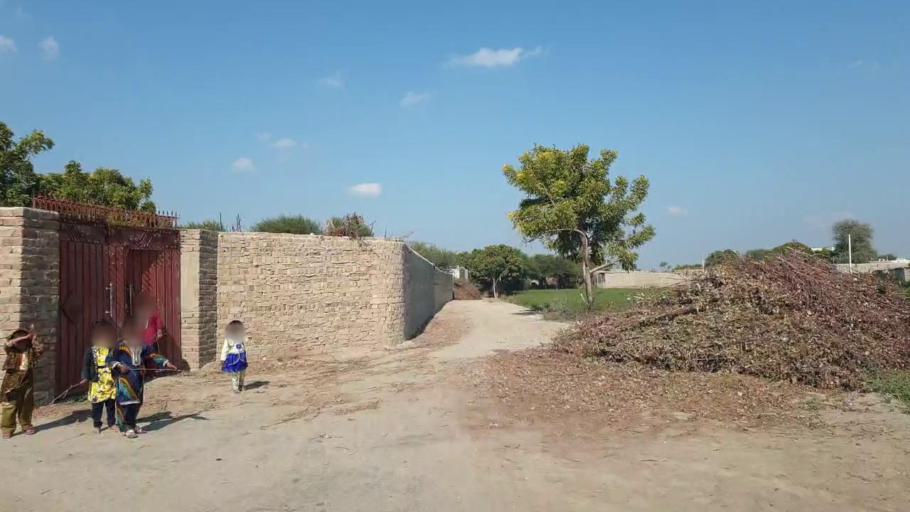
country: PK
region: Sindh
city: Shahpur Chakar
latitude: 26.0625
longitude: 68.5804
